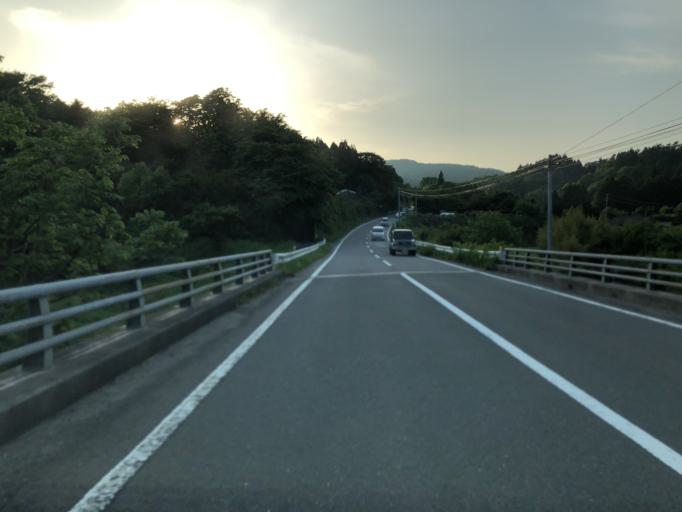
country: JP
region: Fukushima
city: Iwaki
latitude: 37.2394
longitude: 140.9767
